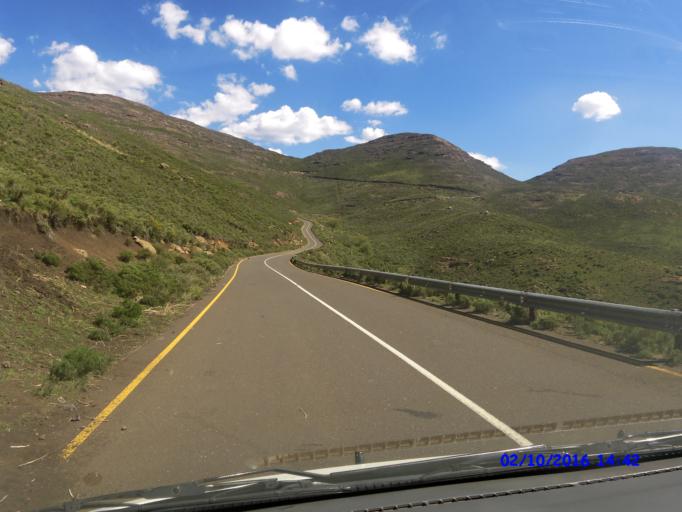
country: LS
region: Maseru
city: Nako
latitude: -29.5297
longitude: 28.0589
